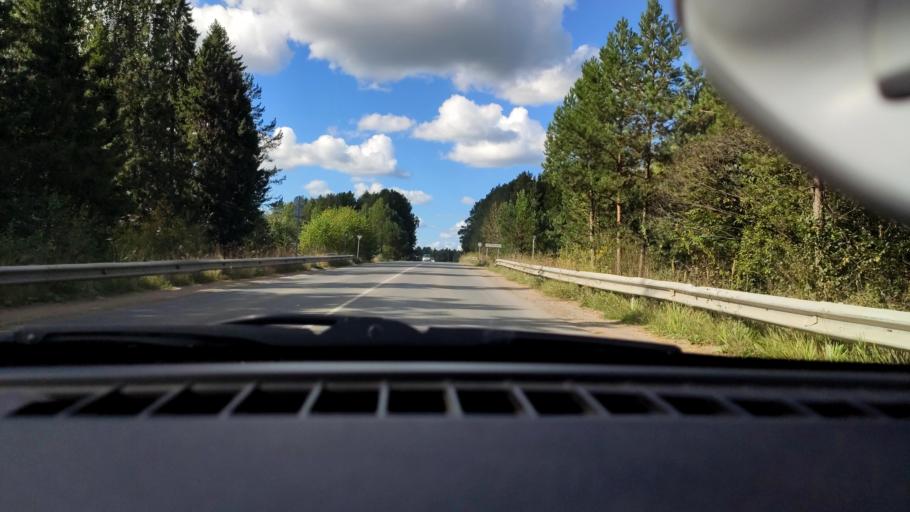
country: RU
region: Perm
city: Ust'-Kachka
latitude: 57.9351
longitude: 55.5261
